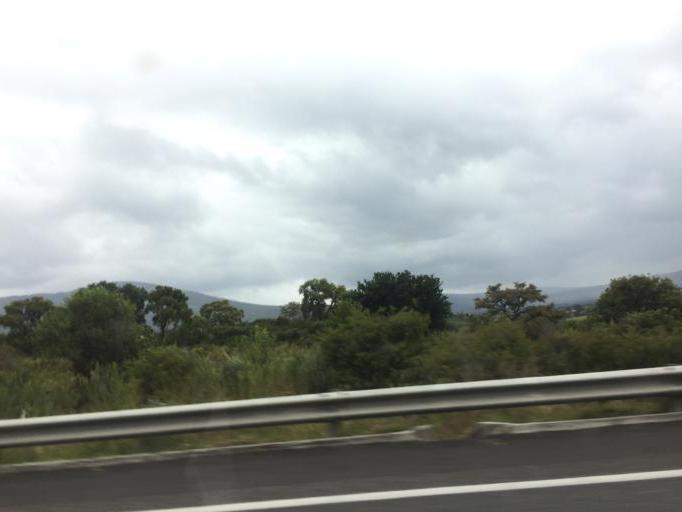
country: MX
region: Jalisco
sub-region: Zapotlanejo
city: La Mezquitera
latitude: 20.5507
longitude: -103.0435
